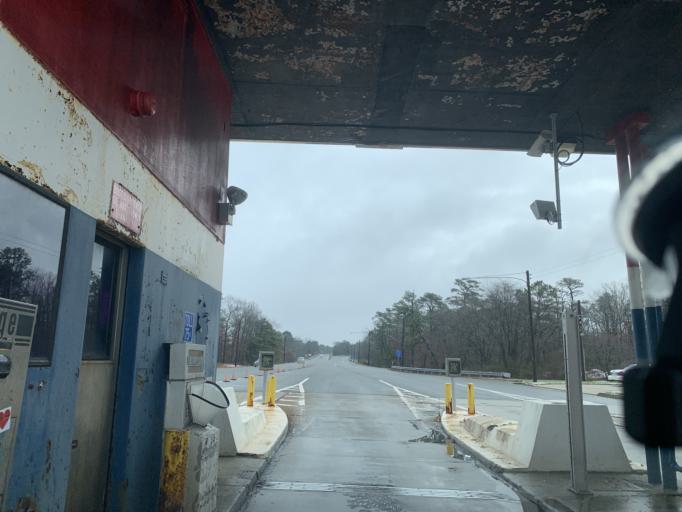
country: US
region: New Jersey
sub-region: Atlantic County
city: Pomona
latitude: 39.4497
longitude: -74.6312
